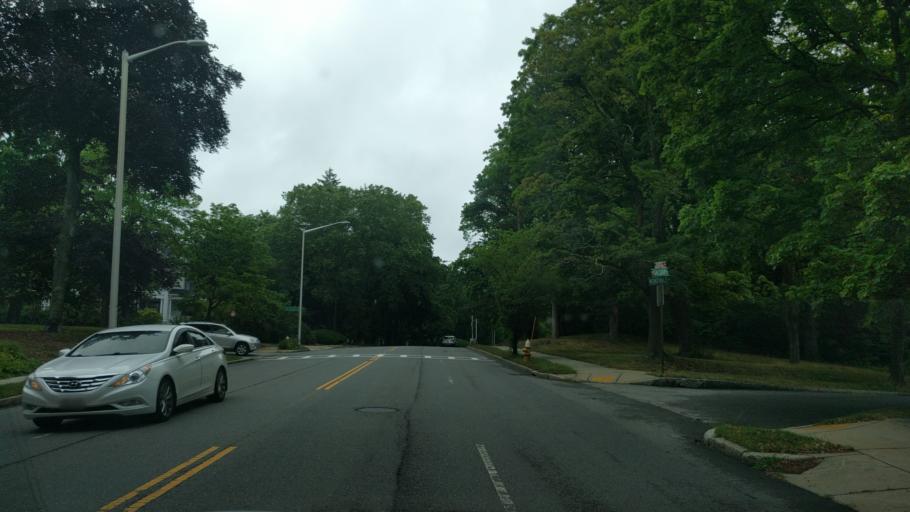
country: US
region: Massachusetts
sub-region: Worcester County
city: Worcester
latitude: 42.2784
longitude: -71.8102
